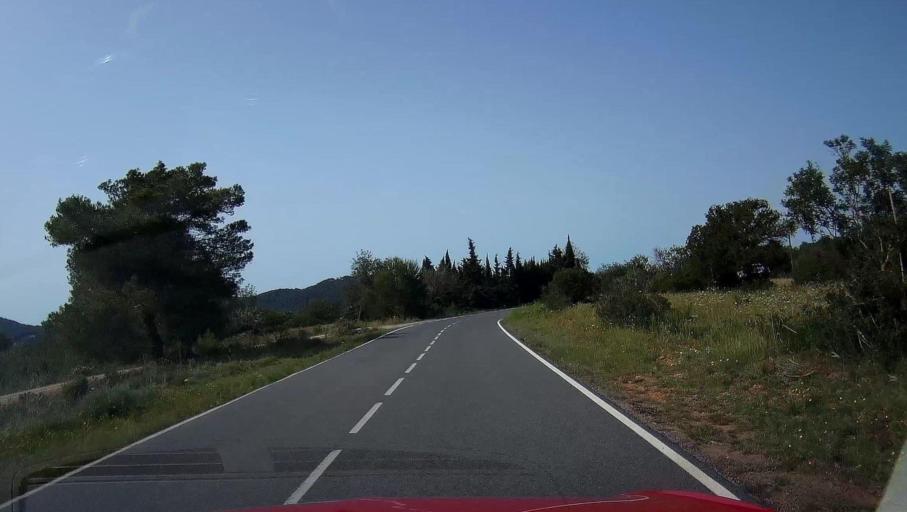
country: ES
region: Balearic Islands
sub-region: Illes Balears
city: Sant Joan de Labritja
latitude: 39.0553
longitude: 1.5808
